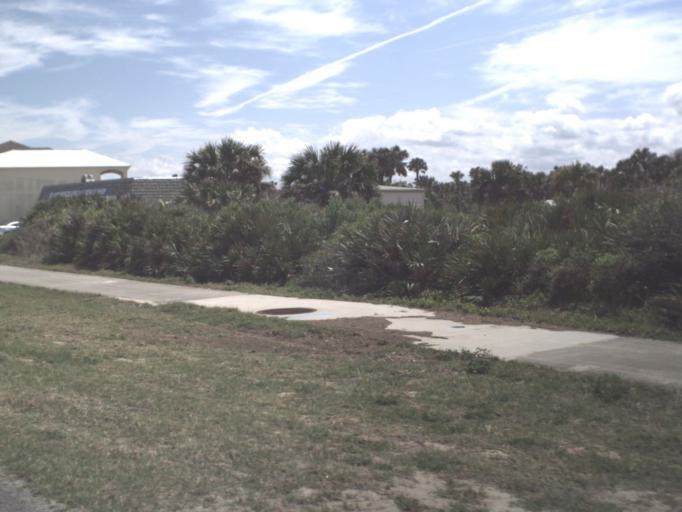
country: US
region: Florida
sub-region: Flagler County
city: Palm Coast
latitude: 29.5459
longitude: -81.1600
